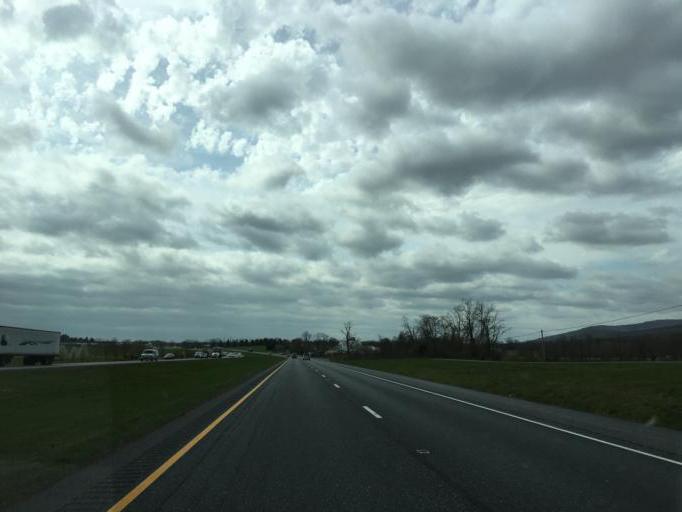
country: US
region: Maryland
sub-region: Frederick County
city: Thurmont
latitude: 39.5584
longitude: -77.4307
